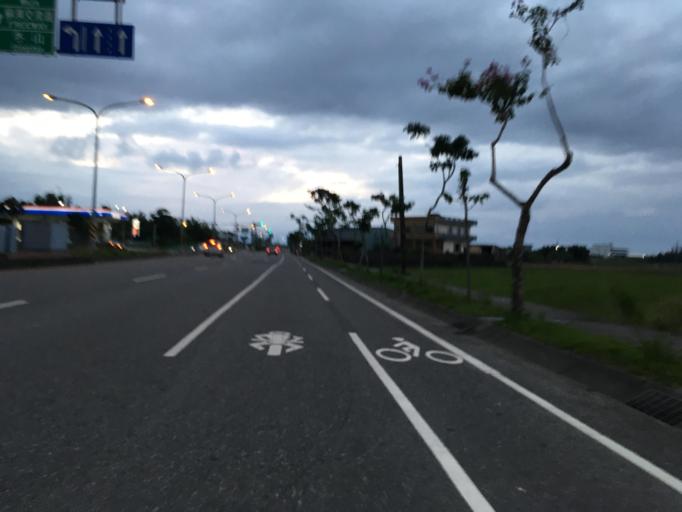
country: TW
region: Taiwan
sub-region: Yilan
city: Yilan
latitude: 24.6252
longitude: 121.8358
